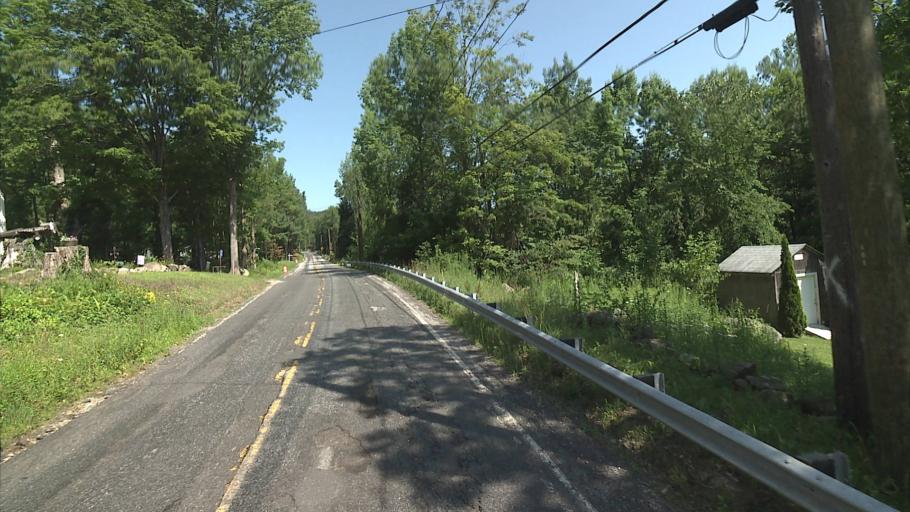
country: US
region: Connecticut
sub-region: Litchfield County
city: Winchester Center
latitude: 41.9255
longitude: -73.2087
